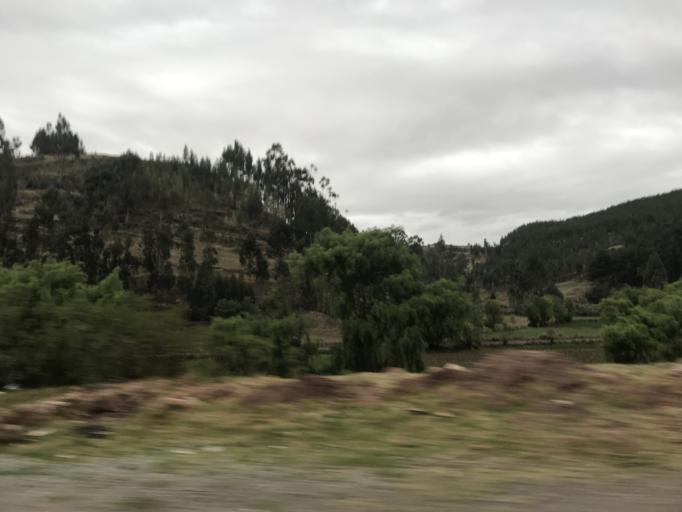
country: PE
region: Cusco
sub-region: Provincia de Anta
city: Huarocondo
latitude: -13.3993
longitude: -72.2105
